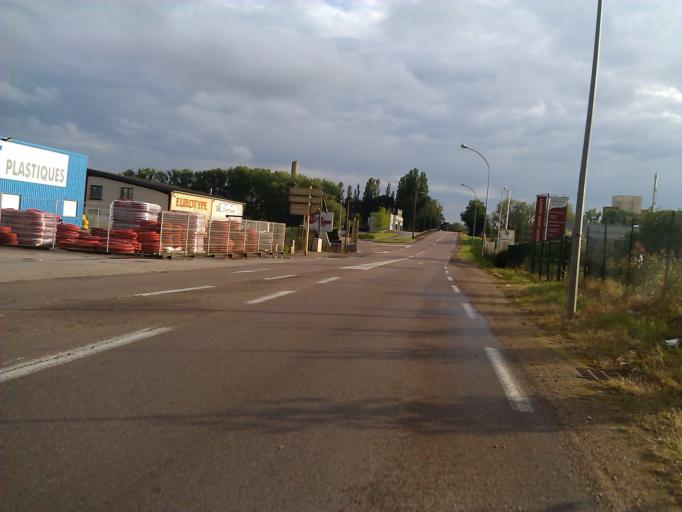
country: FR
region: Bourgogne
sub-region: Departement de Saone-et-Loire
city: Crissey
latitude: 46.8103
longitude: 4.8661
